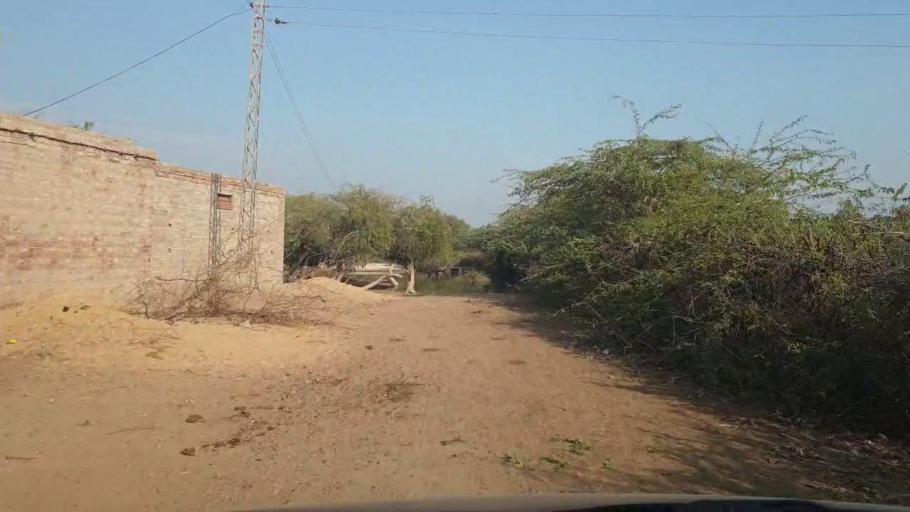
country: PK
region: Sindh
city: Tando Adam
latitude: 25.7257
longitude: 68.6050
